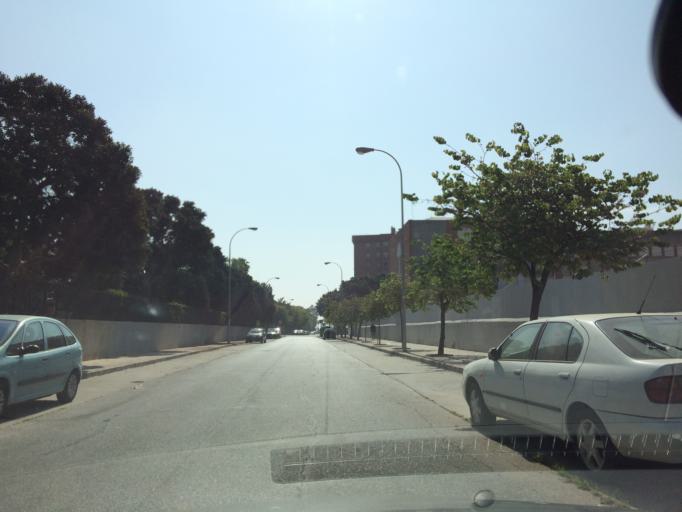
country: ES
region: Andalusia
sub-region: Provincia de Malaga
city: Malaga
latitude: 36.6927
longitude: -4.4471
